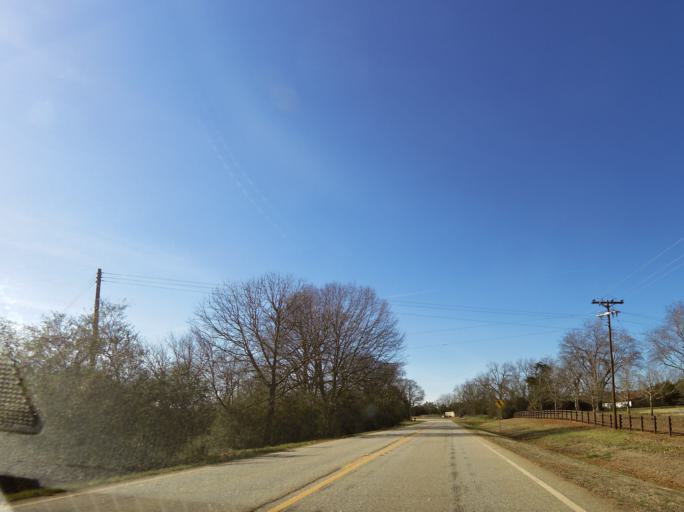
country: US
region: Georgia
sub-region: Crawford County
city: Roberta
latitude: 32.8769
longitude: -84.0748
